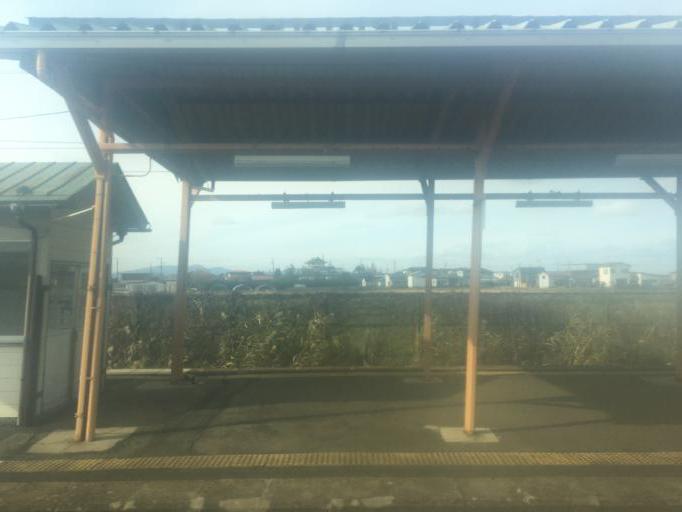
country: JP
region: Akita
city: Tenno
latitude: 39.8992
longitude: 140.0734
